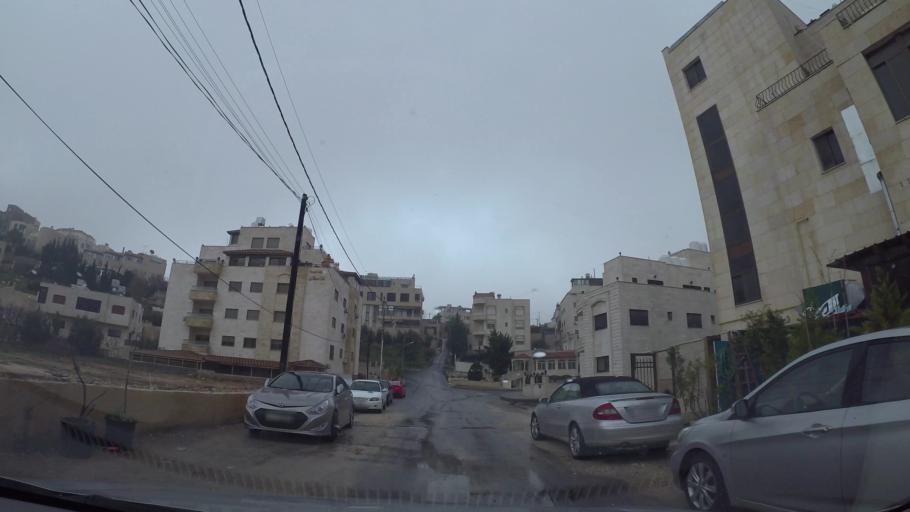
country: JO
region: Amman
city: Al Jubayhah
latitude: 32.0136
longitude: 35.8335
